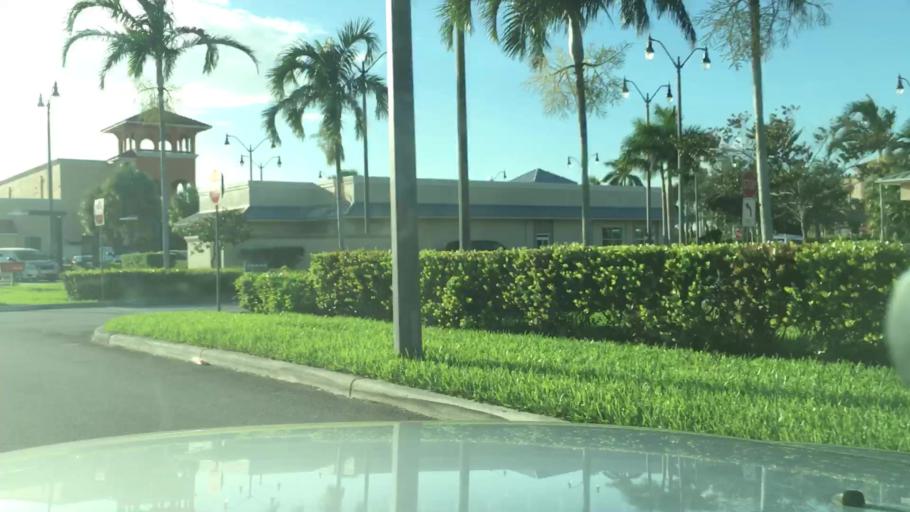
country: US
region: Florida
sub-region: Miami-Dade County
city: Leisure City
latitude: 25.4766
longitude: -80.4341
